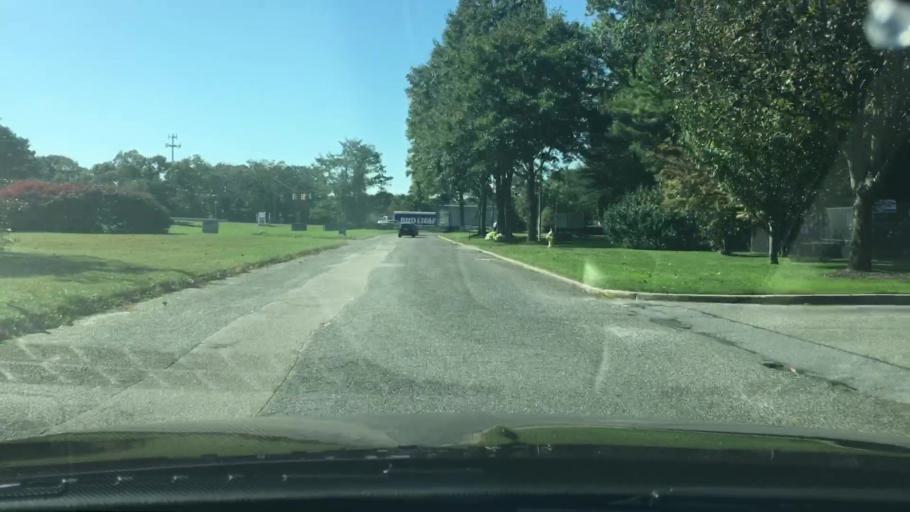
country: US
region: New York
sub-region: Suffolk County
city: Yaphank
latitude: 40.8411
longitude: -72.8864
